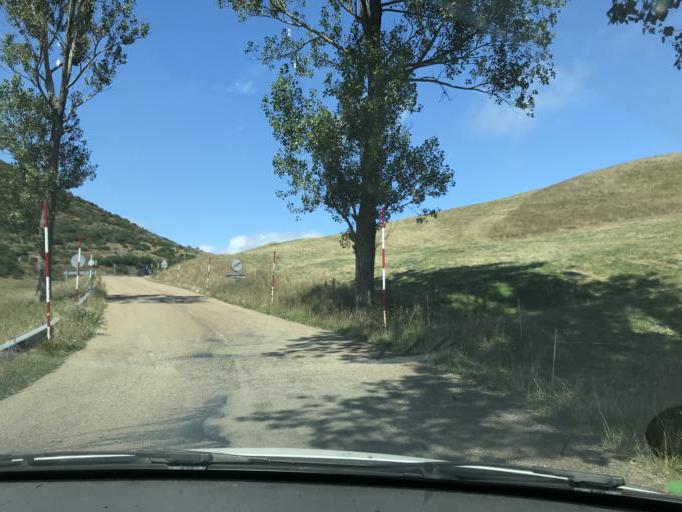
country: ES
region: Castille and Leon
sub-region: Provincia de Palencia
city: Polentinos
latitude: 43.0372
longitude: -4.4569
